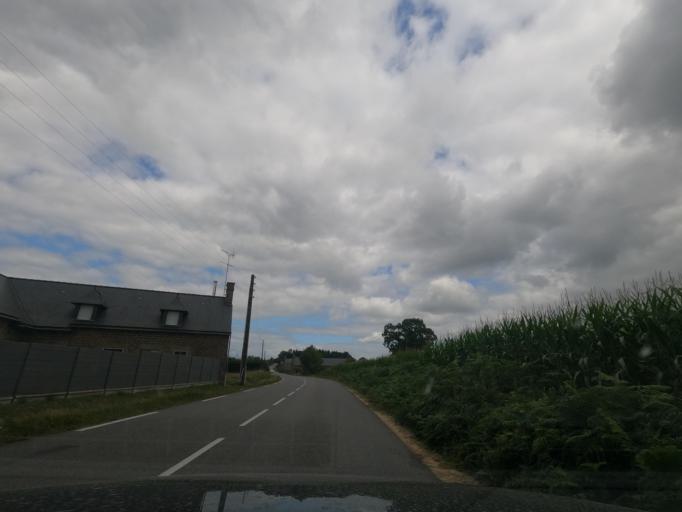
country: FR
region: Brittany
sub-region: Departement d'Ille-et-Vilaine
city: Landean
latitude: 48.4319
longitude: -1.1126
